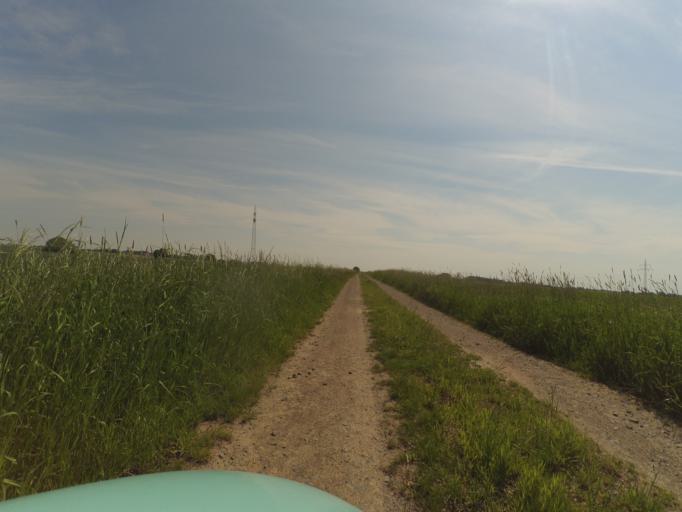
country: DE
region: Lower Saxony
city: Algermissen
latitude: 52.2780
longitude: 9.9954
